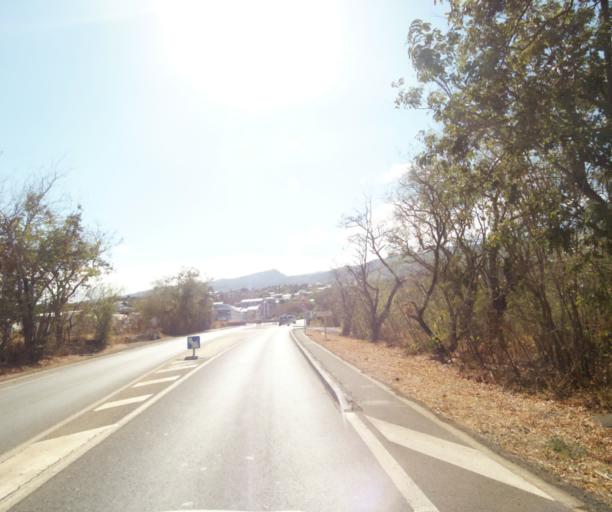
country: RE
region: Reunion
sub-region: Reunion
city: Le Port
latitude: -20.9810
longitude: 55.3144
